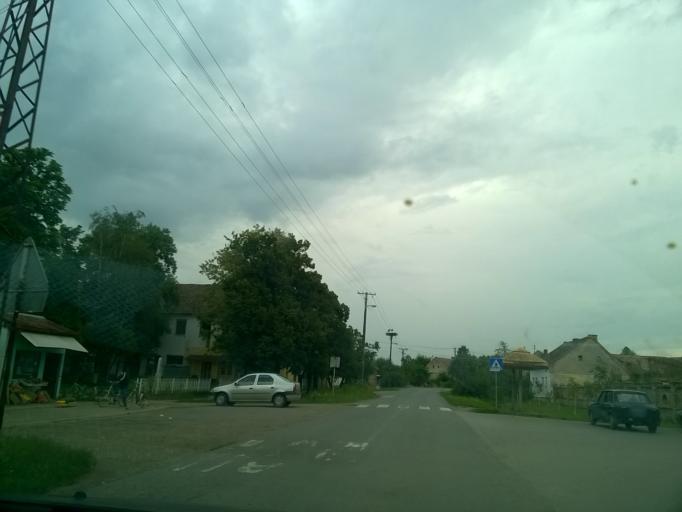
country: RS
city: Tomasevac
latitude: 45.2681
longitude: 20.6206
